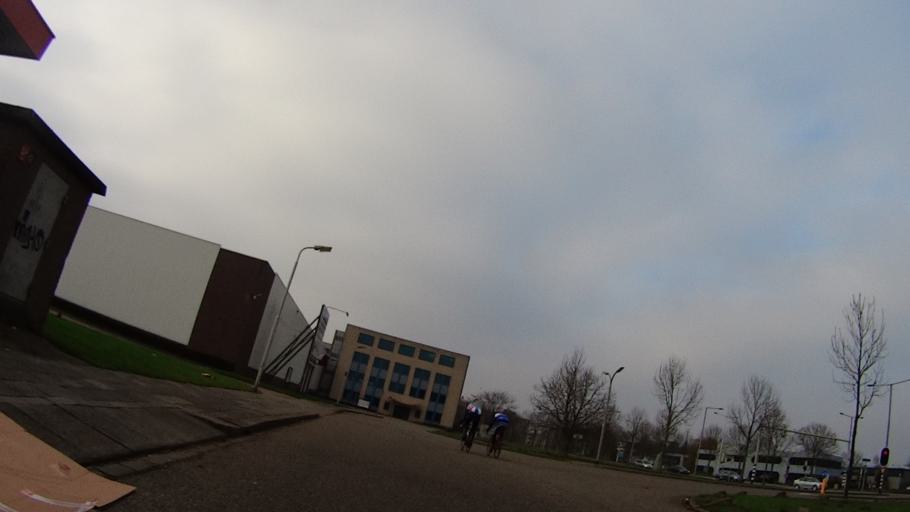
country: NL
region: Utrecht
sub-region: Gemeente Amersfoort
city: Randenbroek
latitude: 52.1722
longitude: 5.4176
